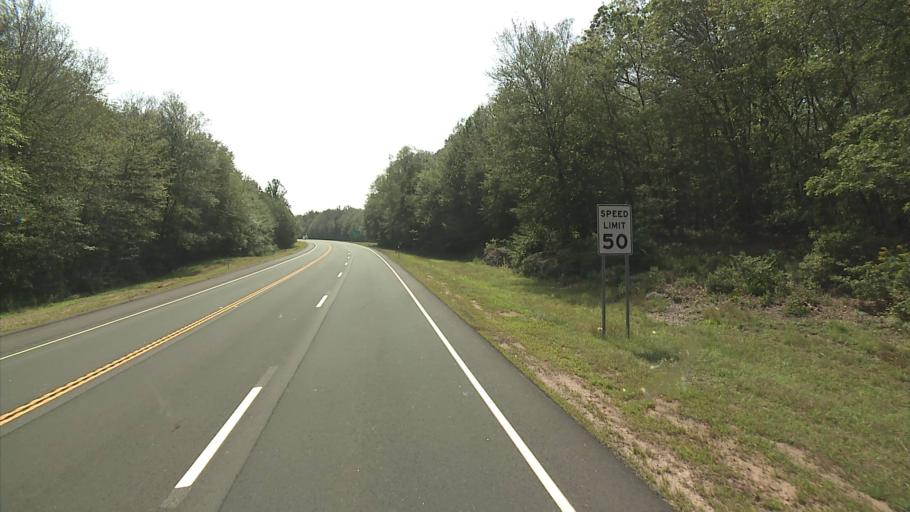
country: US
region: Connecticut
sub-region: Middlesex County
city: East Haddam
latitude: 41.4353
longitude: -72.4887
